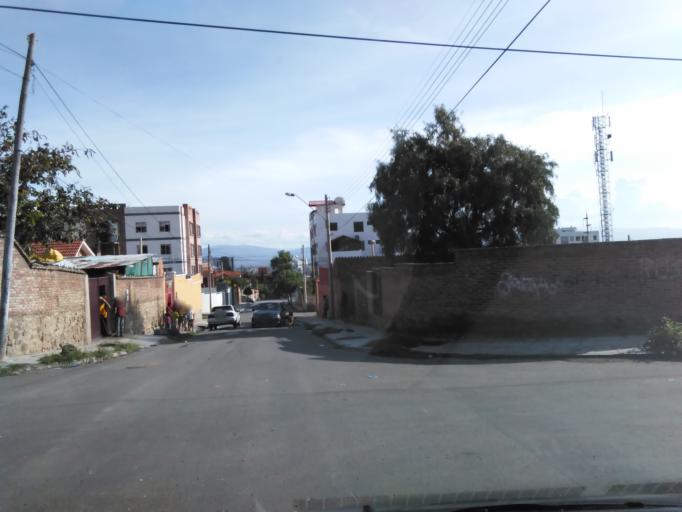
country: BO
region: Cochabamba
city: Cochabamba
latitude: -17.3668
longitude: -66.1467
